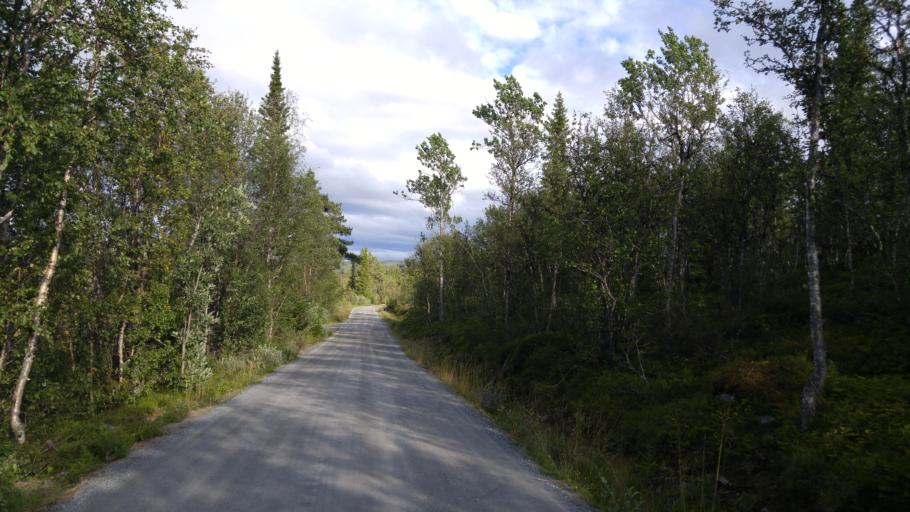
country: NO
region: Buskerud
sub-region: Hemsedal
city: Troim
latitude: 60.8473
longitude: 8.7206
